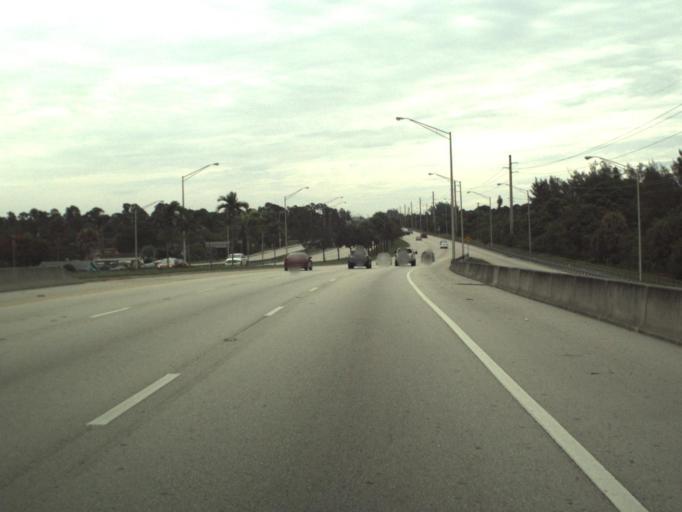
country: US
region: Florida
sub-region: Palm Beach County
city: Lake Belvedere Estates
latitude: 26.6787
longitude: -80.1443
